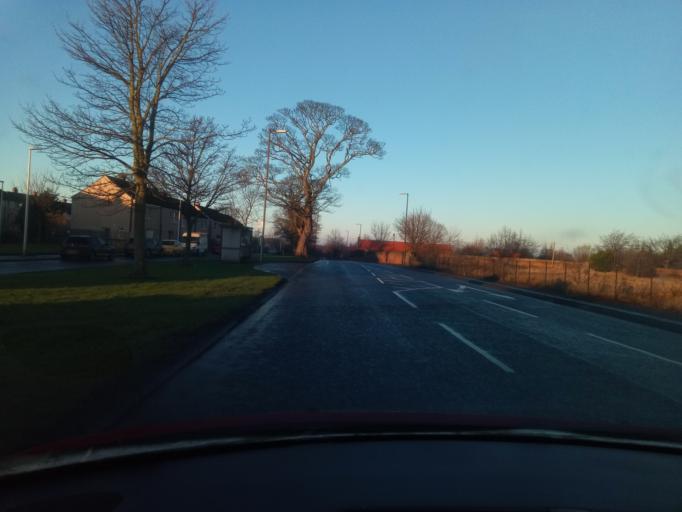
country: GB
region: Scotland
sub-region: East Lothian
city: Musselburgh
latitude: 55.9429
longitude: -3.0162
